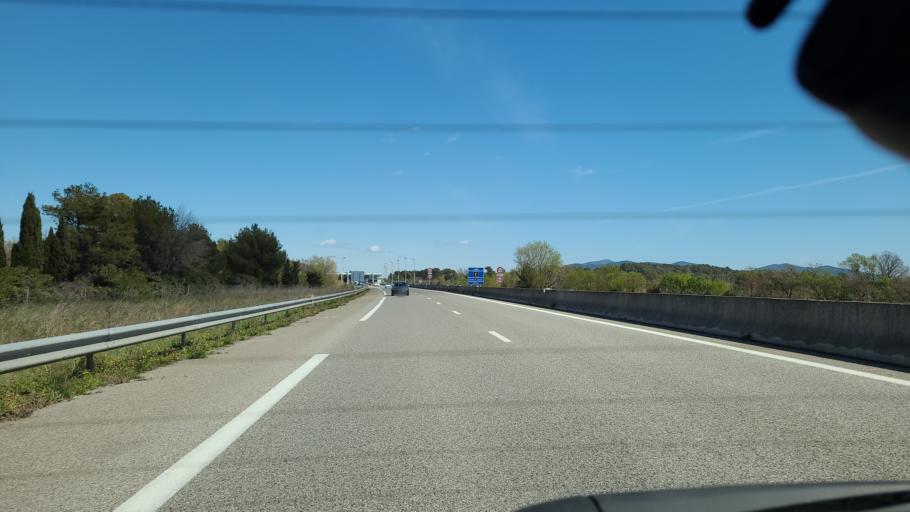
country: FR
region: Provence-Alpes-Cote d'Azur
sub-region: Departement du Var
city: Puget-Ville
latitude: 43.2553
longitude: 6.1175
